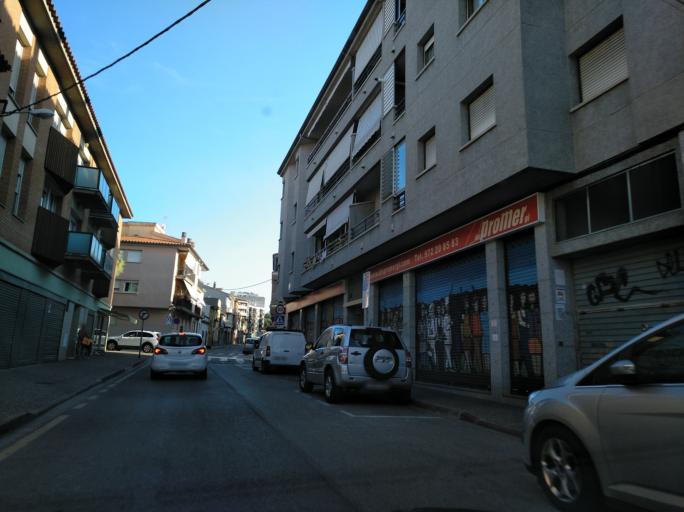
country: ES
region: Catalonia
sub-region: Provincia de Girona
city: Girona
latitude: 41.9702
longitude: 2.8216
